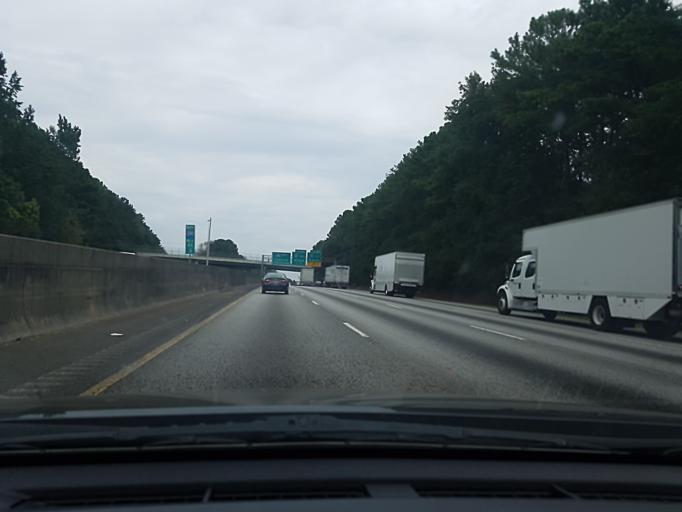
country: US
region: Georgia
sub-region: DeKalb County
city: Panthersville
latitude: 33.7079
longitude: -84.2473
